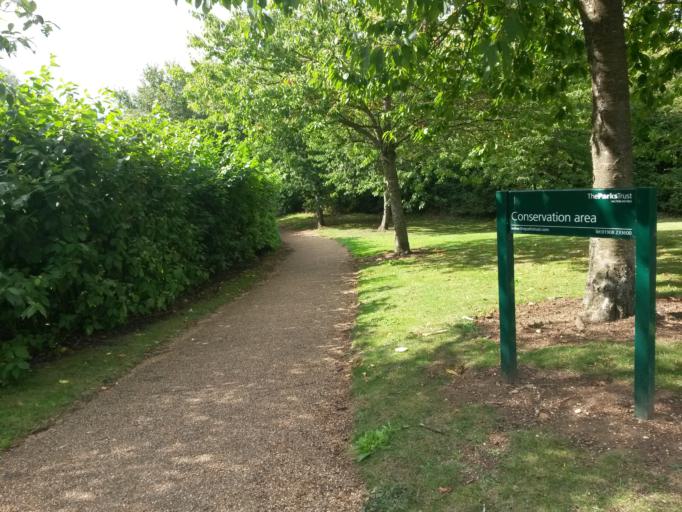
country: GB
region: England
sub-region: Milton Keynes
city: Simpson
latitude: 52.0032
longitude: -0.7034
